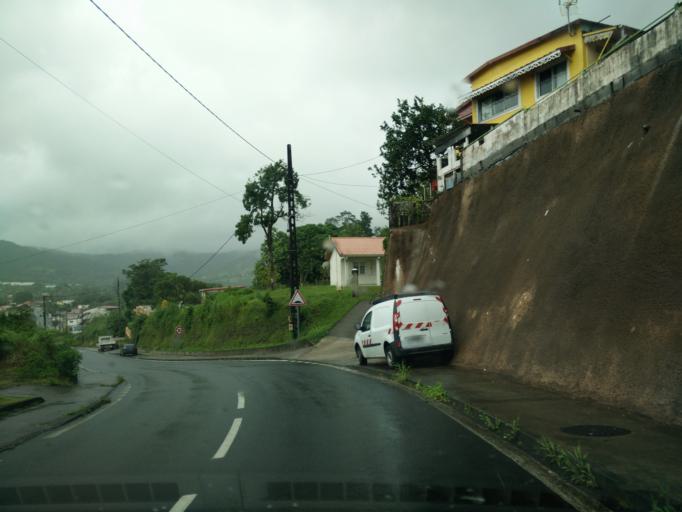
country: MQ
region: Martinique
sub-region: Martinique
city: Le Morne-Rouge
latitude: 14.7684
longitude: -61.1264
